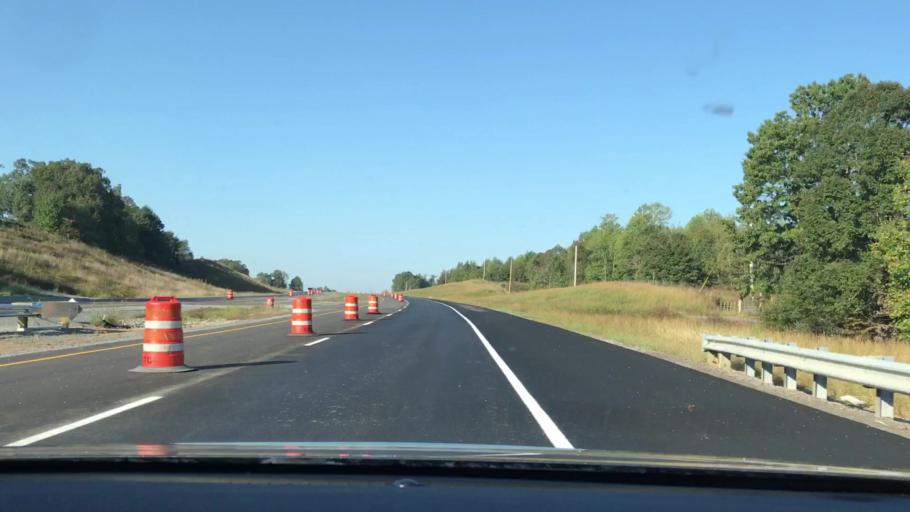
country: US
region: Kentucky
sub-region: Trigg County
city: Cadiz
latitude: 36.8417
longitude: -87.8340
